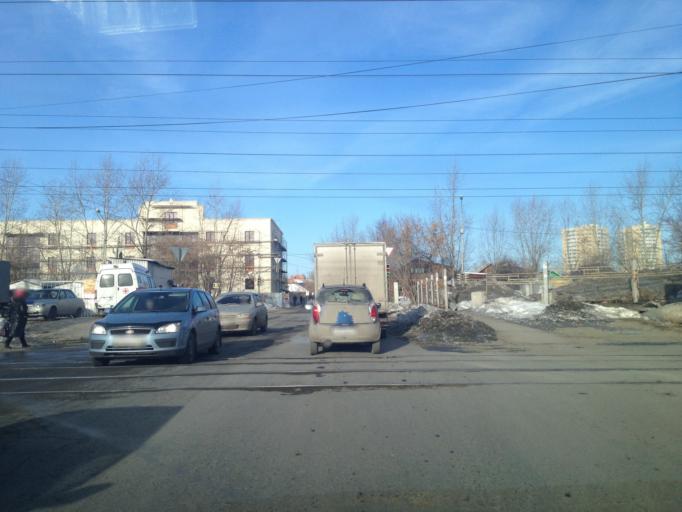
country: RU
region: Sverdlovsk
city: Sovkhoznyy
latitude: 56.7692
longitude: 60.5965
